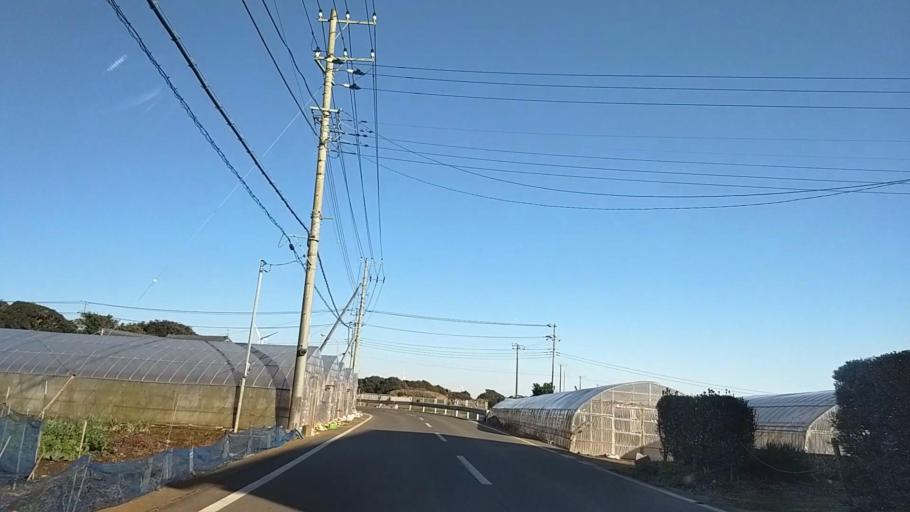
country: JP
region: Chiba
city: Asahi
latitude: 35.7159
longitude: 140.7305
